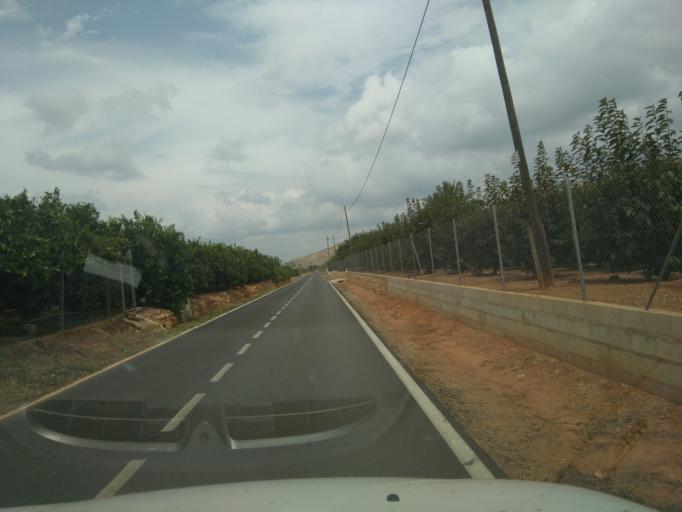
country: ES
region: Valencia
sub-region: Provincia de Valencia
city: Rafelguaraf
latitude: 39.0774
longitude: -0.4251
